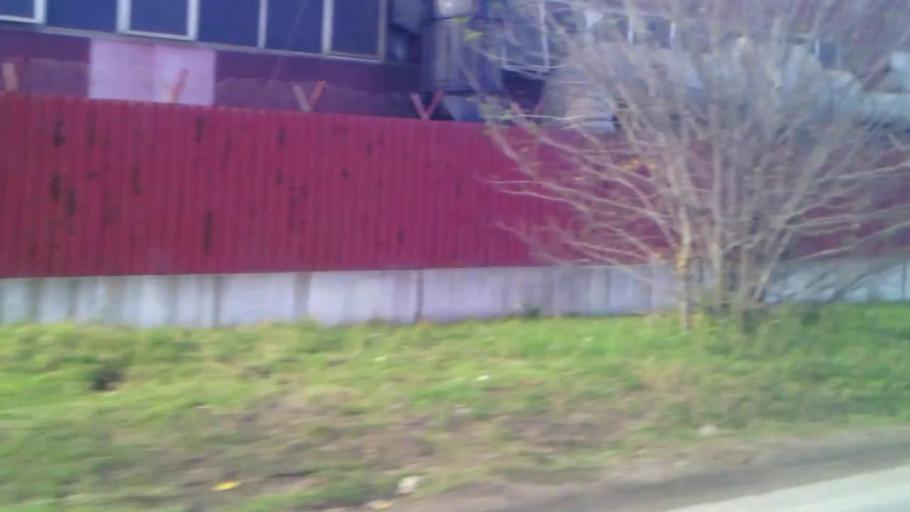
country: RO
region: Ilfov
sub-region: Comuna Popesti-Leordeni
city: Popesti-Leordeni
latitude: 44.3571
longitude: 26.1519
